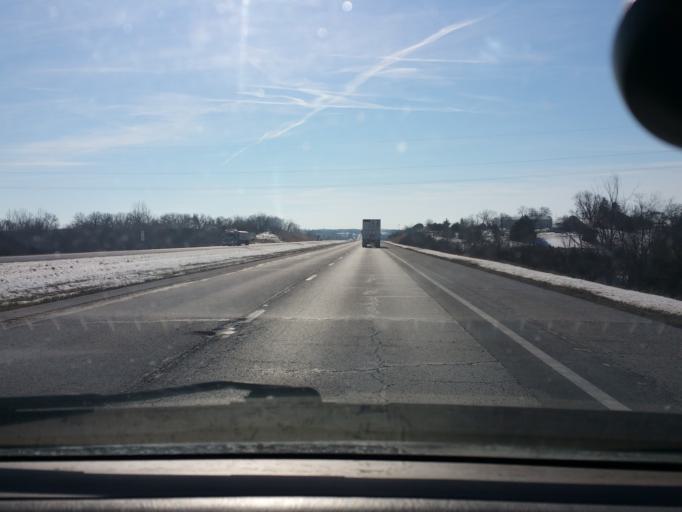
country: US
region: Missouri
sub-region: Harrison County
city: Bethany
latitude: 40.2515
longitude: -94.0131
